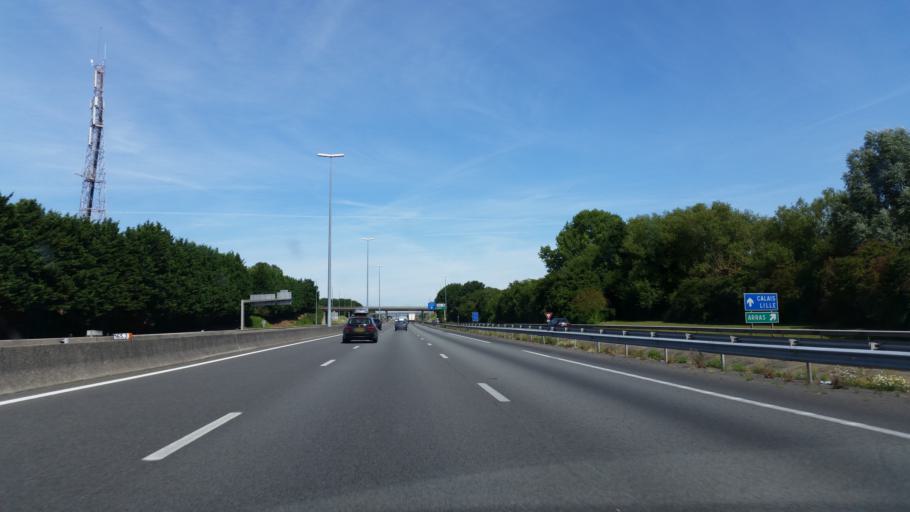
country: FR
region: Nord-Pas-de-Calais
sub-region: Departement du Pas-de-Calais
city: Feuchy
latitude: 50.2641
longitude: 2.8652
